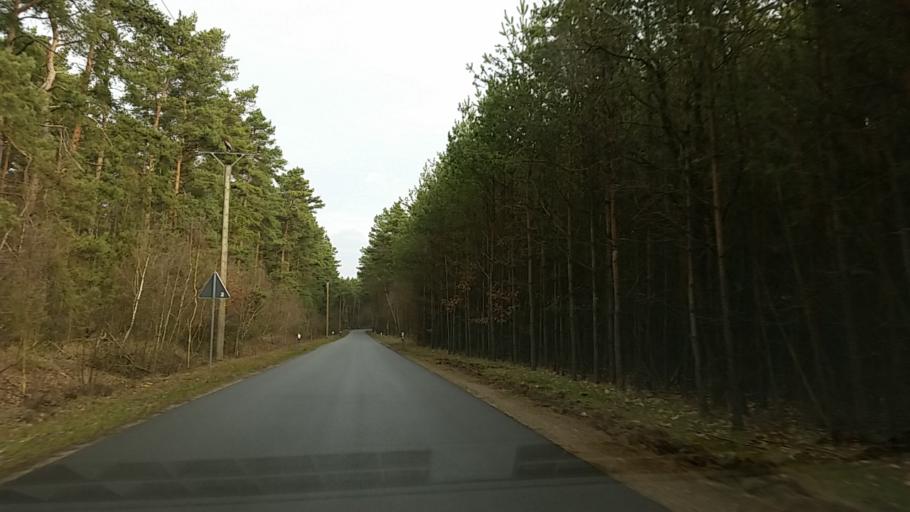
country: DE
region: Lower Saxony
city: Bodenteich
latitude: 52.8096
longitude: 10.7196
